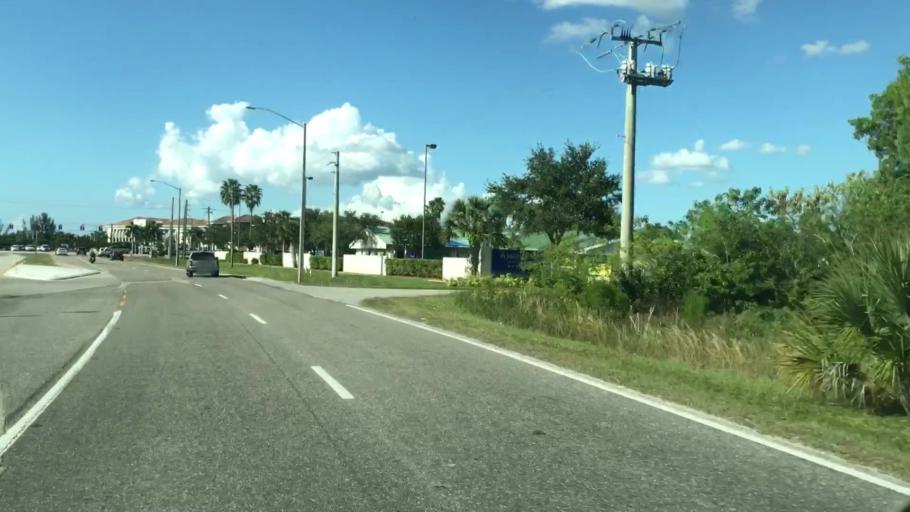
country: US
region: Florida
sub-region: Lee County
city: Fort Myers
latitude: 26.6082
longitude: -81.8197
